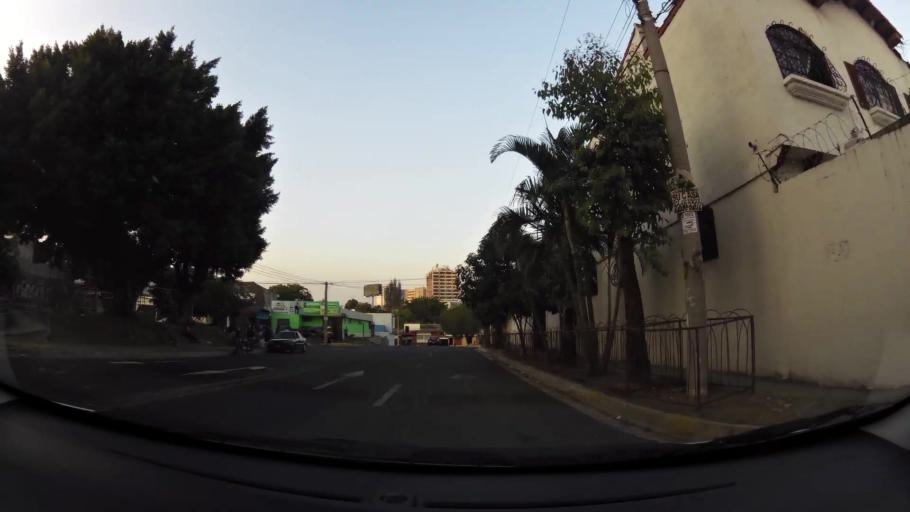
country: SV
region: San Salvador
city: San Salvador
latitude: 13.7080
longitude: -89.2079
